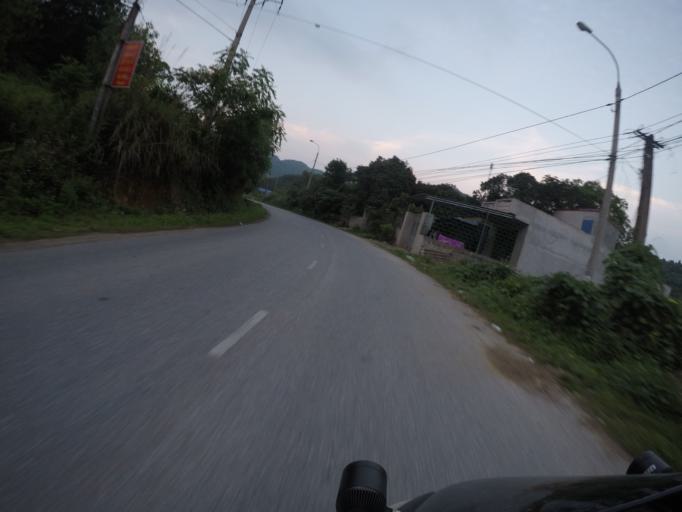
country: VN
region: Thai Nguyen
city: Chua Hang
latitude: 21.5855
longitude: 105.7062
